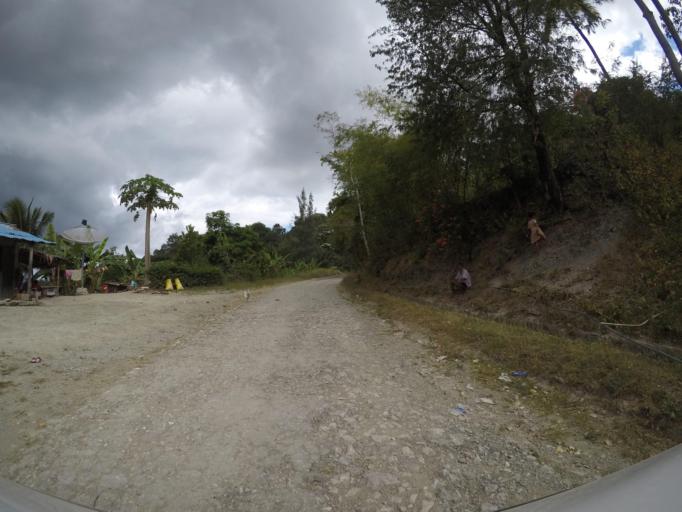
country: TL
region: Baucau
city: Baucau
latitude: -8.6264
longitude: 126.6561
